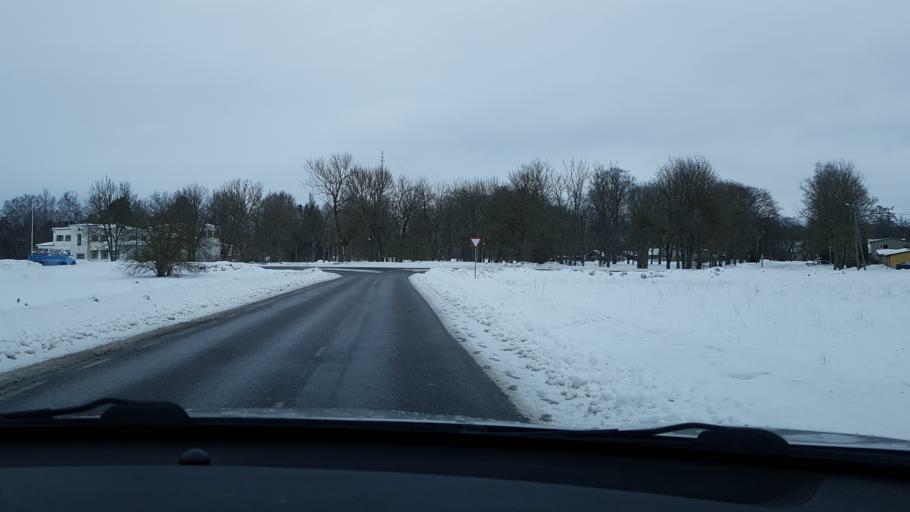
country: EE
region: Jaervamaa
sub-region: Jaerva-Jaani vald
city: Jarva-Jaani
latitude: 59.1393
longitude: 25.7531
